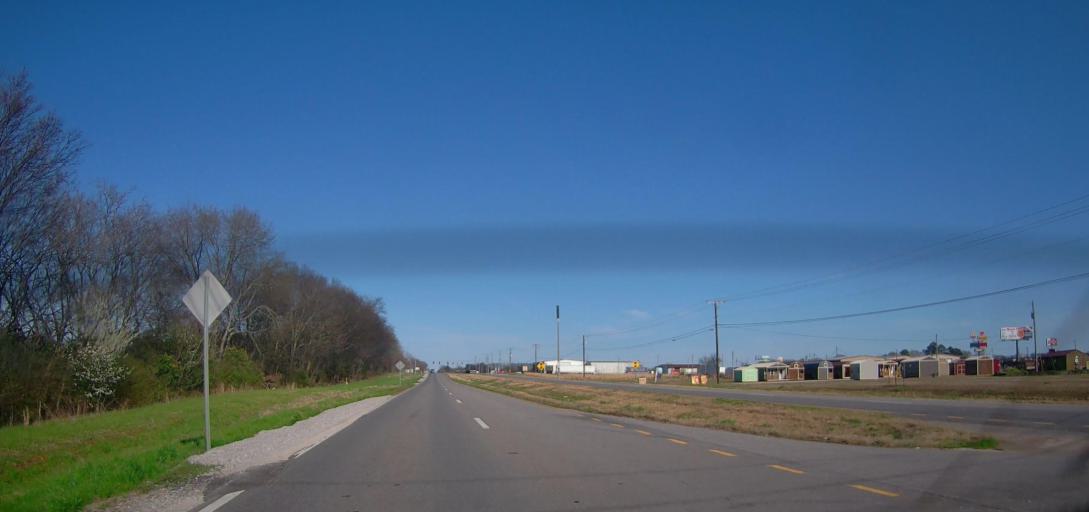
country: US
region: Alabama
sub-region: Colbert County
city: Muscle Shoals
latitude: 34.7007
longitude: -87.6390
